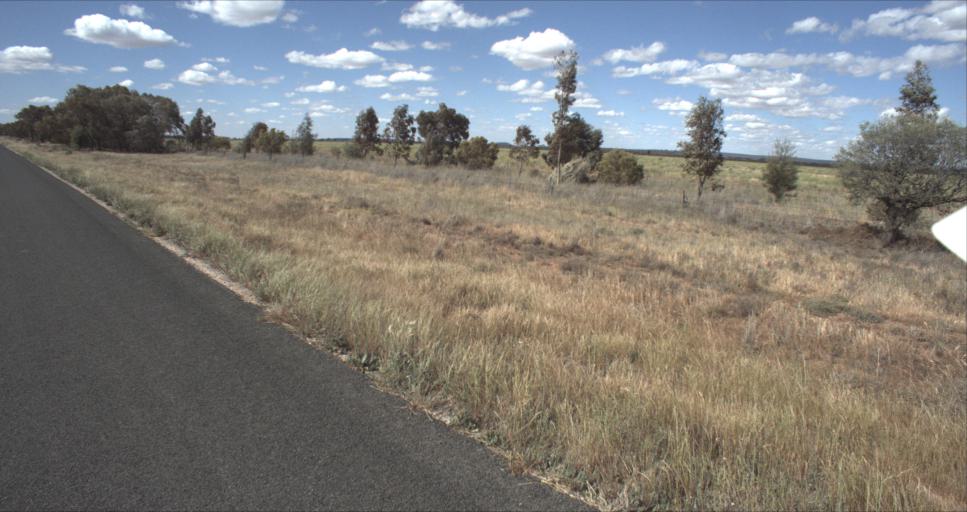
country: AU
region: New South Wales
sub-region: Leeton
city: Leeton
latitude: -34.4389
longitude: 146.2568
